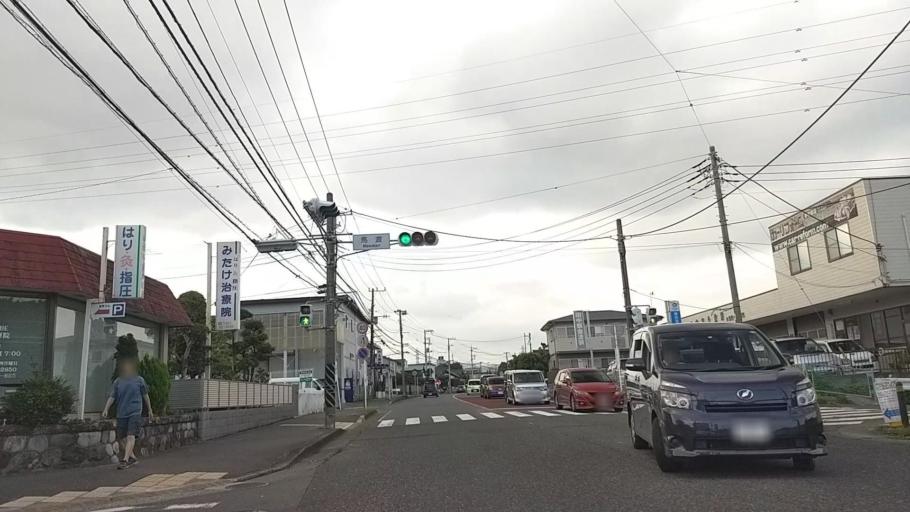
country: JP
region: Kanagawa
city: Isehara
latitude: 35.3822
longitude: 139.3166
